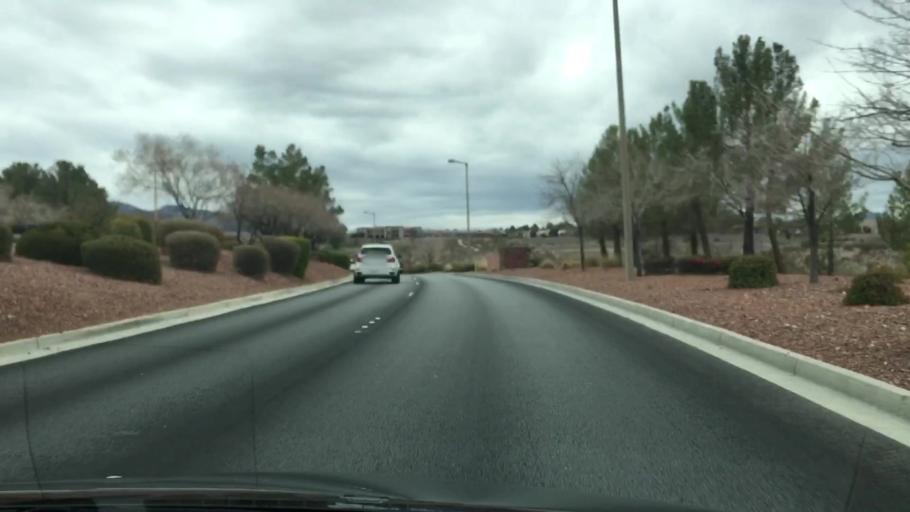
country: US
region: Nevada
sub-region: Clark County
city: Whitney
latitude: 35.9647
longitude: -115.0981
